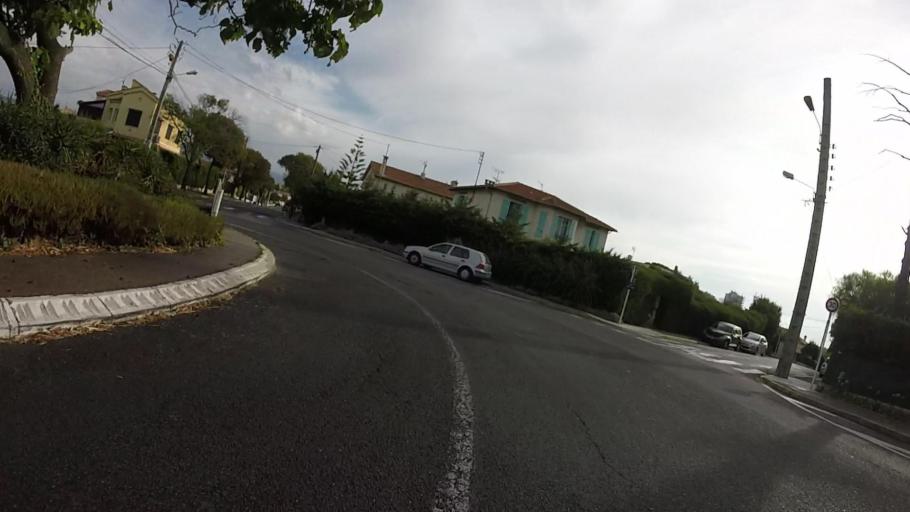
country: FR
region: Provence-Alpes-Cote d'Azur
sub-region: Departement des Alpes-Maritimes
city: Antibes
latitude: 43.5851
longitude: 7.1073
